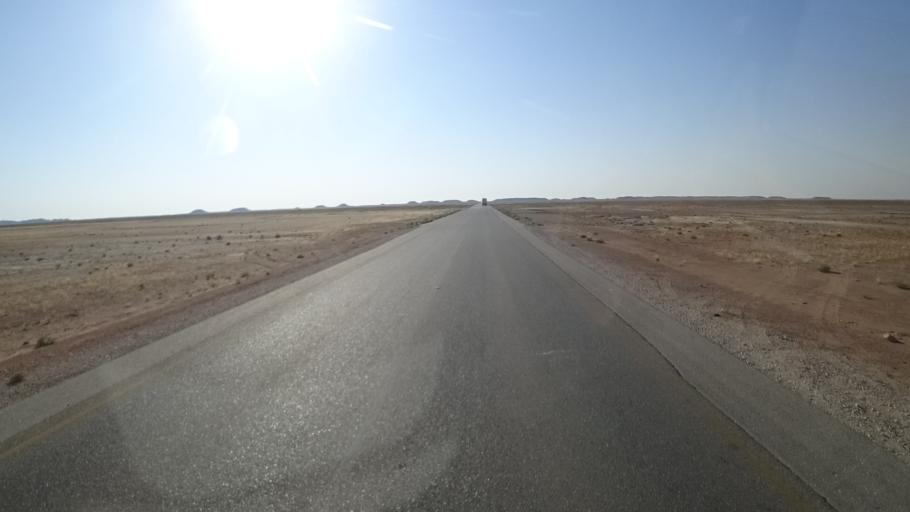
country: OM
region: Zufar
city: Salalah
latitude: 17.6424
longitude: 53.8384
